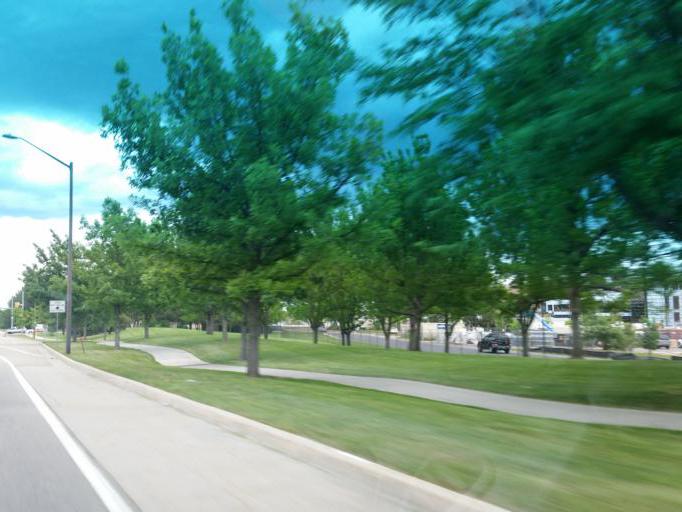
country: US
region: Colorado
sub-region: Larimer County
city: Fort Collins
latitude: 40.5248
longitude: -105.0202
